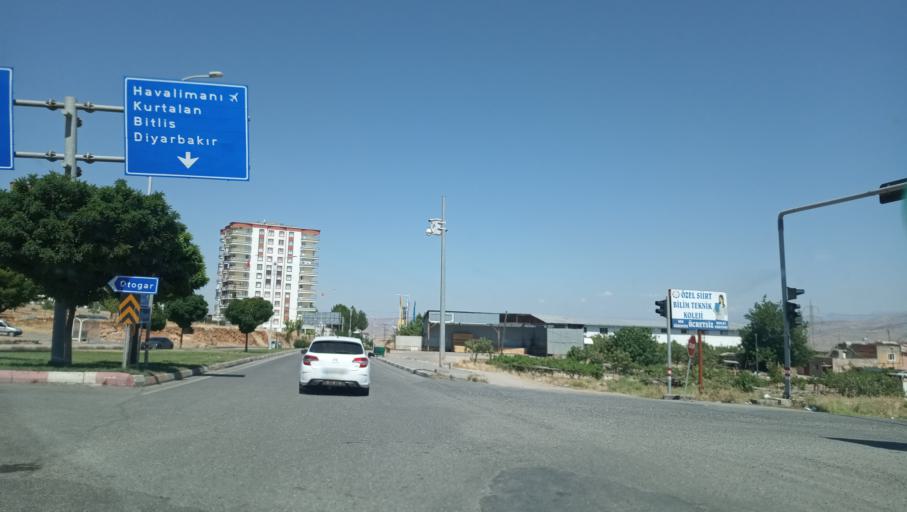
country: TR
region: Siirt
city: Civankan
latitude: 37.9492
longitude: 41.8937
